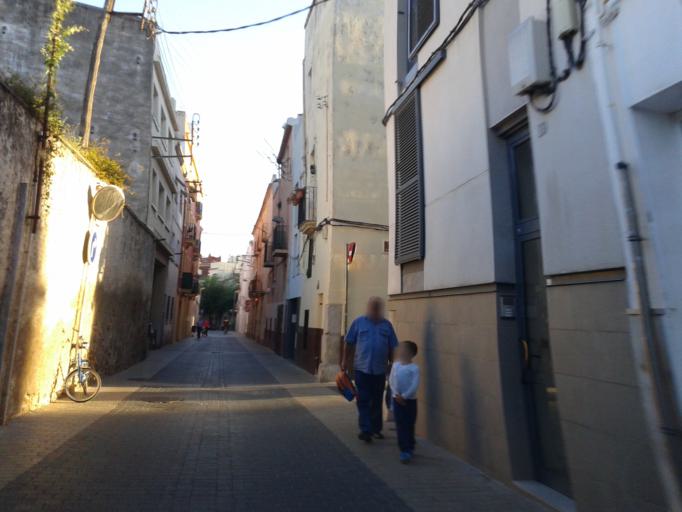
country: ES
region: Catalonia
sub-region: Provincia de Barcelona
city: Vilanova i la Geltru
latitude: 41.2259
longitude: 1.7215
